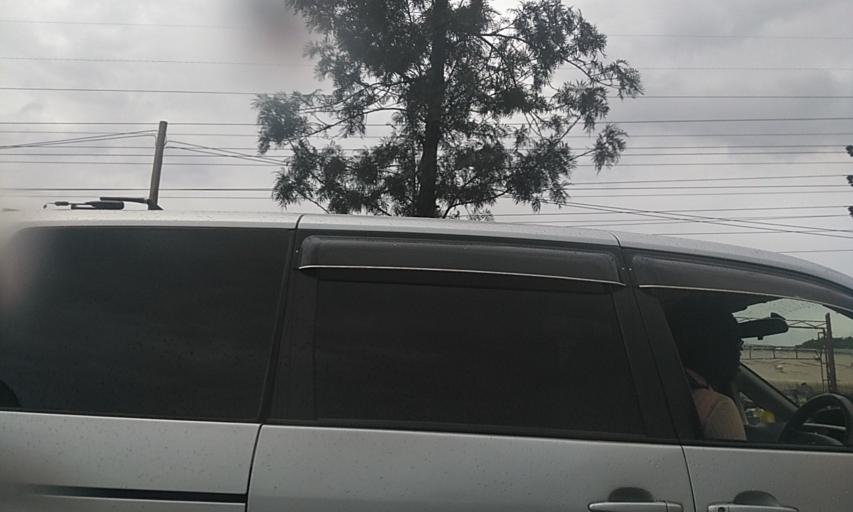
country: UG
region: Central Region
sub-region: Kampala District
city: Kampala
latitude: 0.3277
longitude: 32.6114
